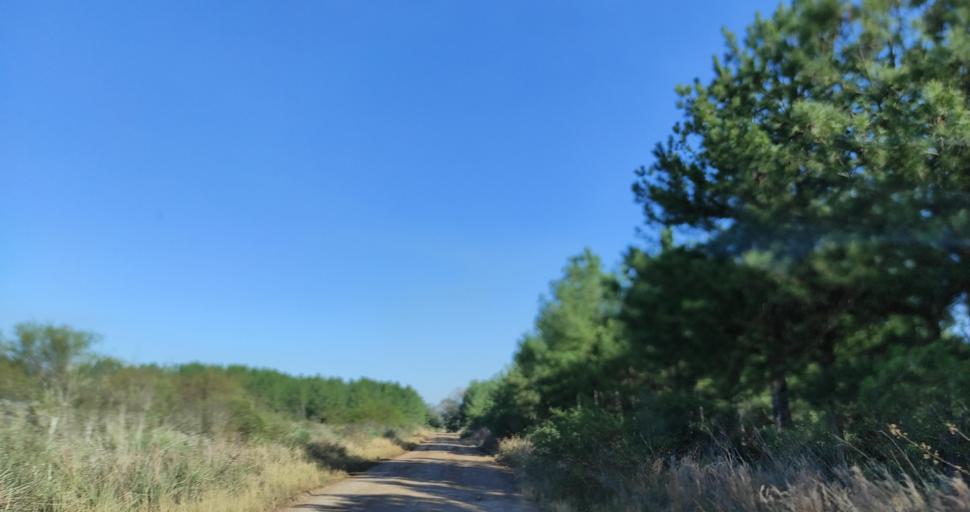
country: AR
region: Misiones
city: Cerro Cora
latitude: -27.6502
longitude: -55.6577
